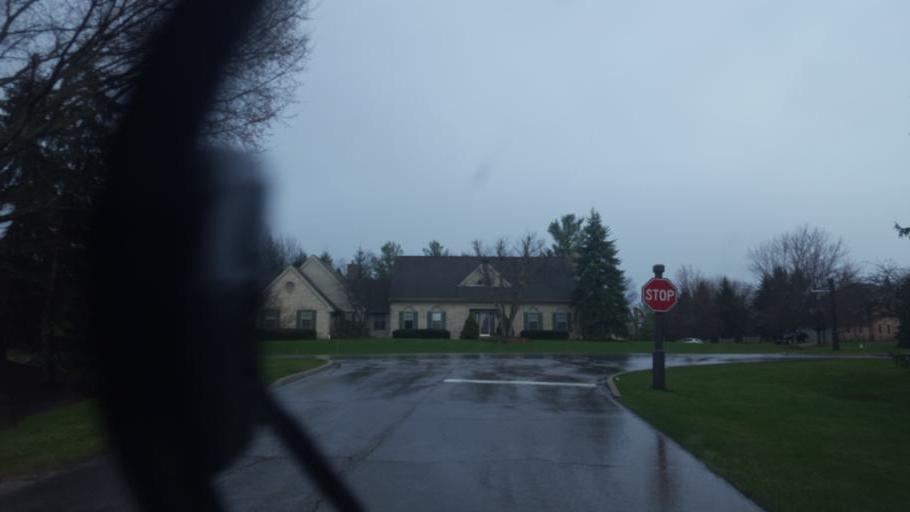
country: US
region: Ohio
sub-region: Delaware County
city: Powell
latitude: 40.1605
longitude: -83.0566
